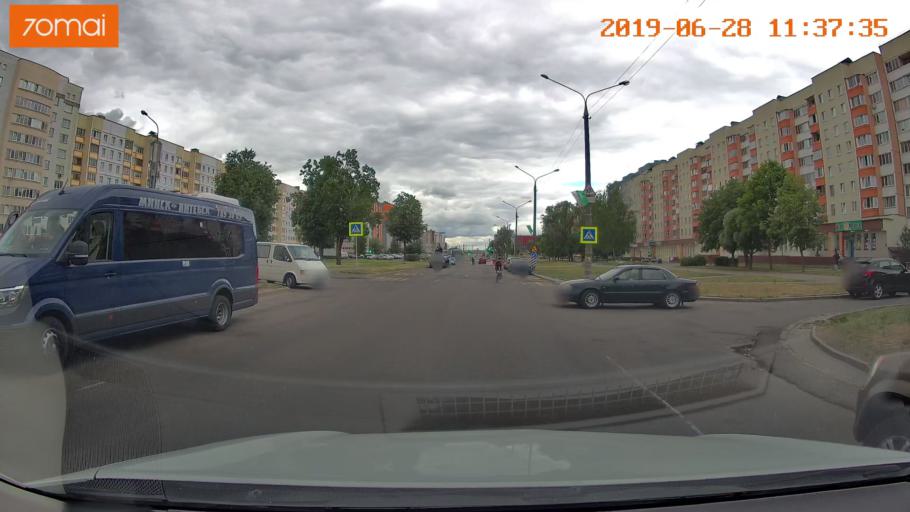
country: BY
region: Minsk
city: Minsk
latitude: 53.8840
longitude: 27.5517
